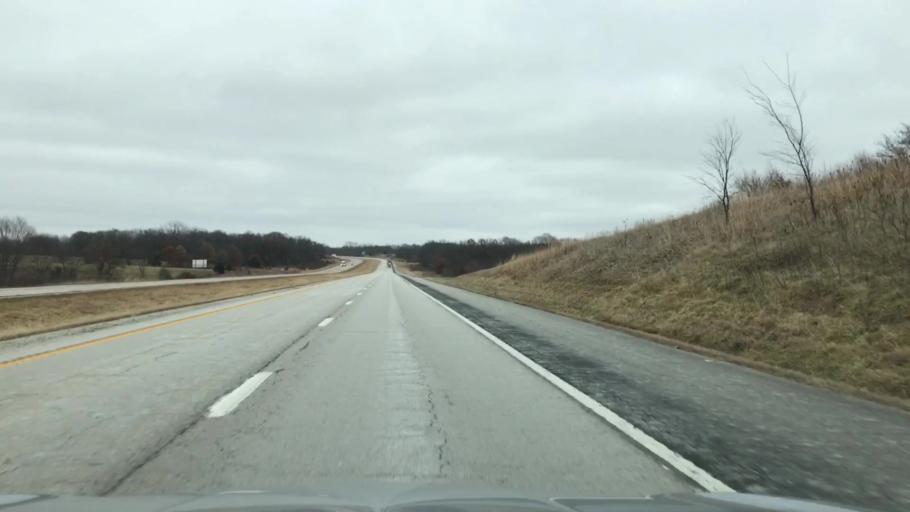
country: US
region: Missouri
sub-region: Caldwell County
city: Hamilton
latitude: 39.7399
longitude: -94.0350
